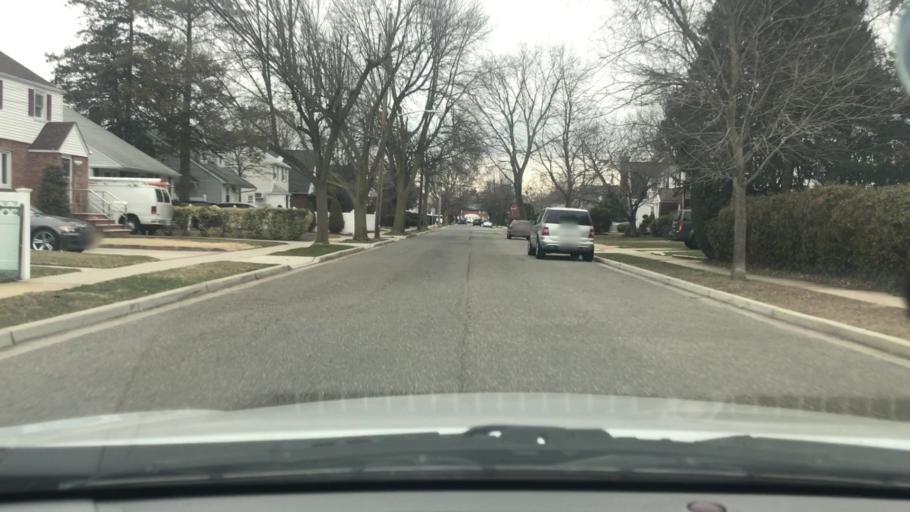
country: US
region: New York
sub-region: Nassau County
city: Uniondale
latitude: 40.7066
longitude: -73.6030
